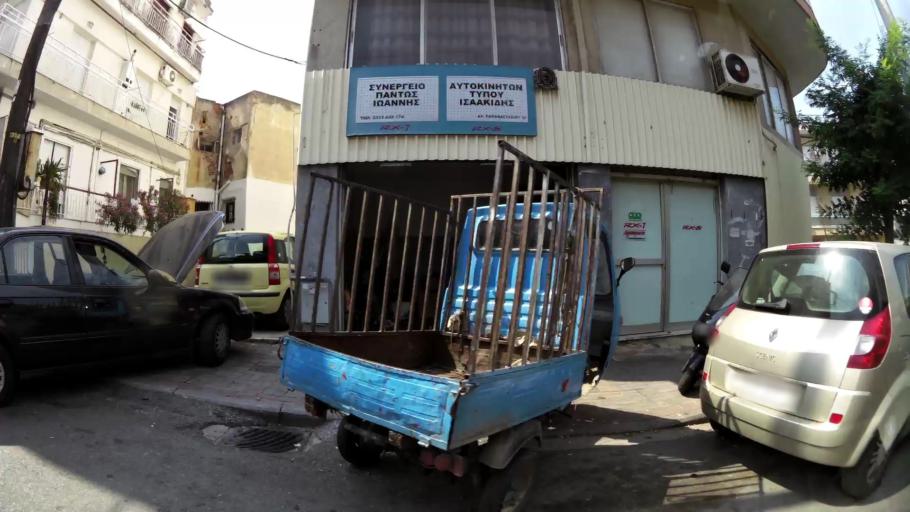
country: GR
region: Central Macedonia
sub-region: Nomos Thessalonikis
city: Sykies
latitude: 40.6472
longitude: 22.9418
